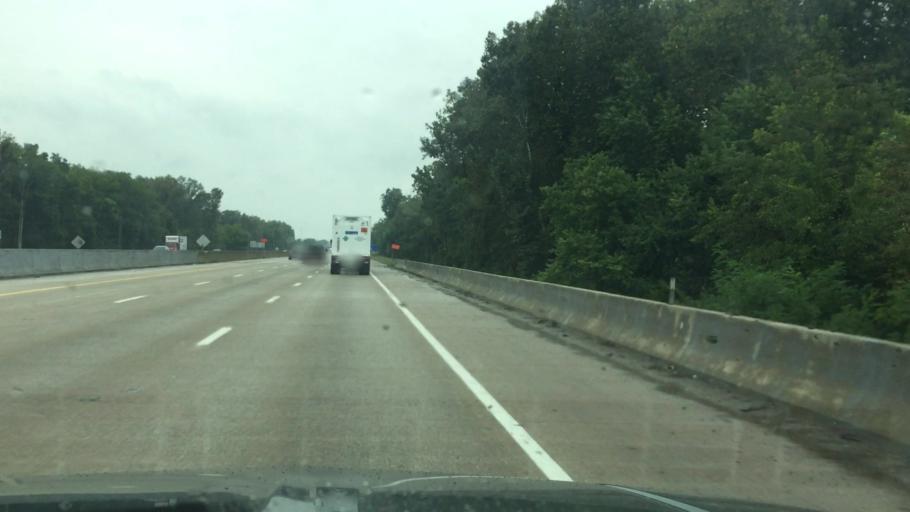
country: US
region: Ohio
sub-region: Clark County
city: Crystal Lakes
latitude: 39.8647
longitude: -84.0188
